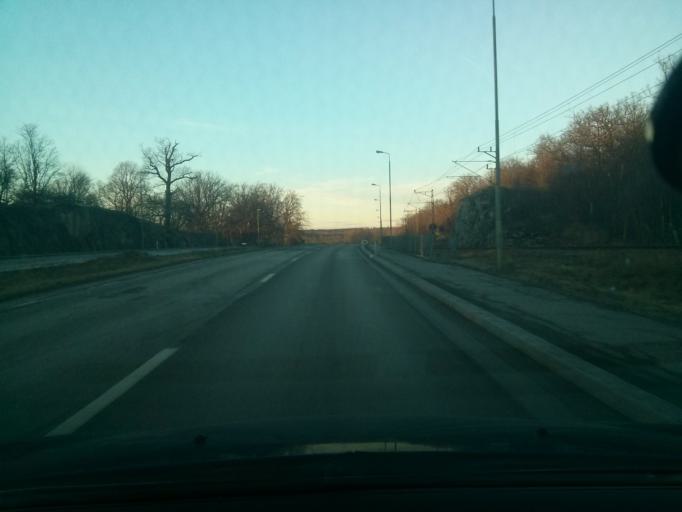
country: SE
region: Blekinge
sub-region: Karlskrona Kommun
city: Rodeby
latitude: 56.2057
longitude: 15.6039
